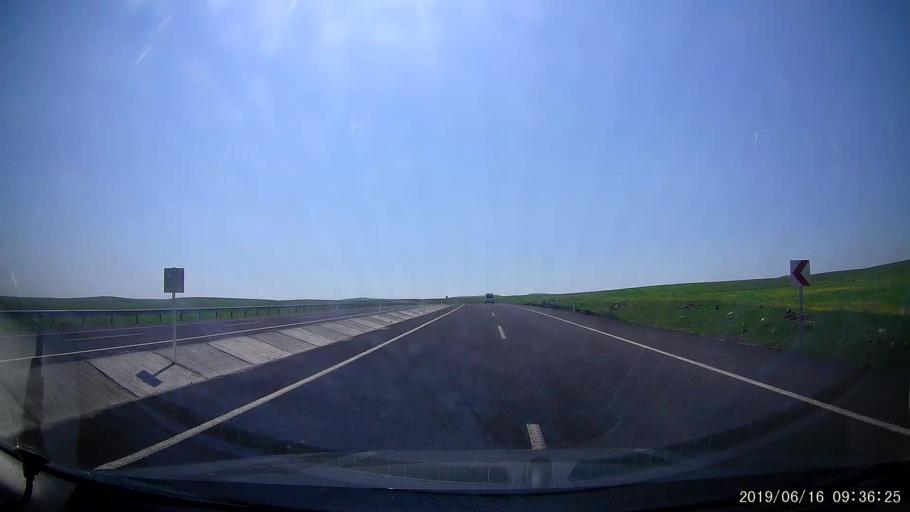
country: TR
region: Kars
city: Kars
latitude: 40.5581
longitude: 43.1721
